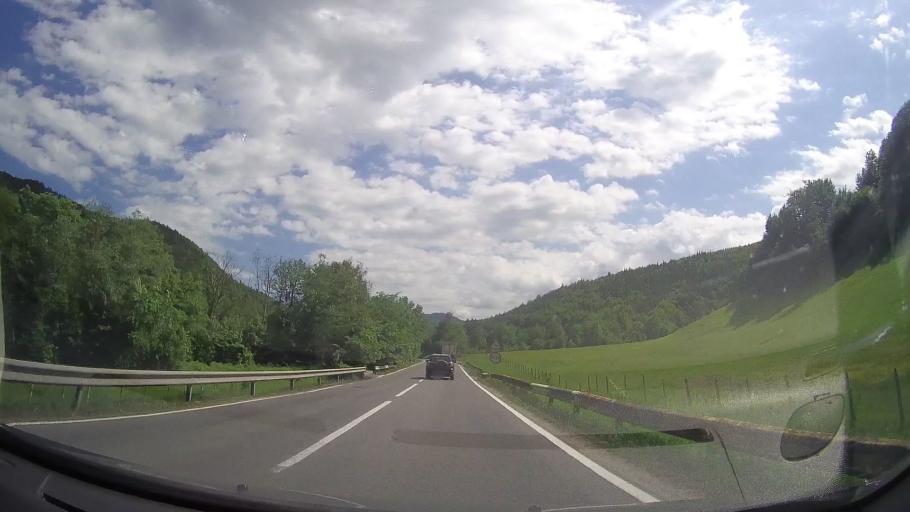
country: RO
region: Prahova
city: Maneciu
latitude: 45.3856
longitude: 25.9294
